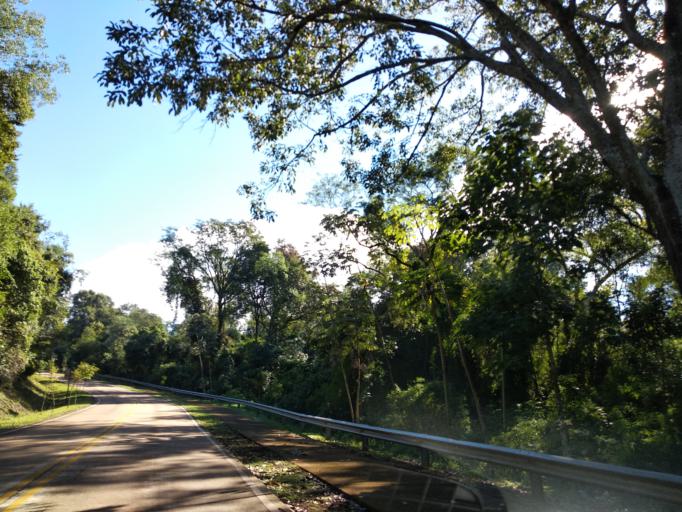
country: AR
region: Misiones
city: Cerro Cora
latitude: -27.4542
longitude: -55.5722
